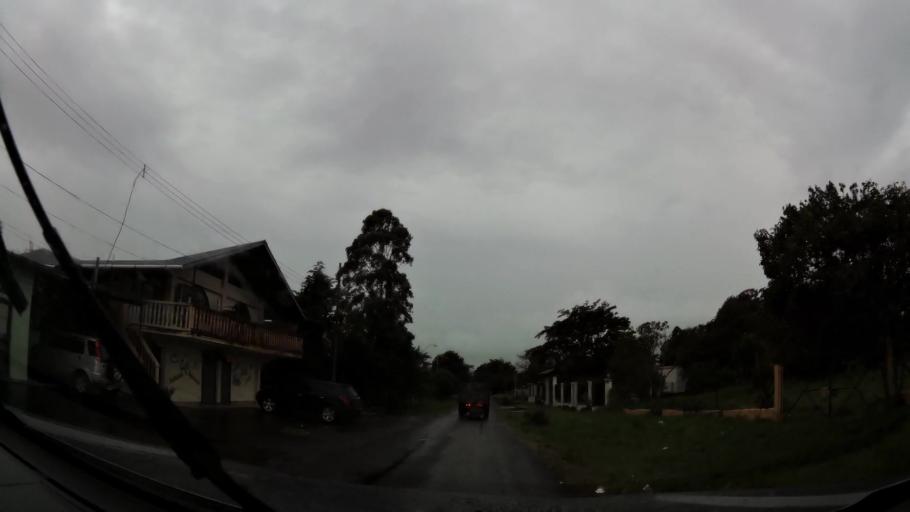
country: PA
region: Chiriqui
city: Volcan
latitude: 8.7882
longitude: -82.6504
